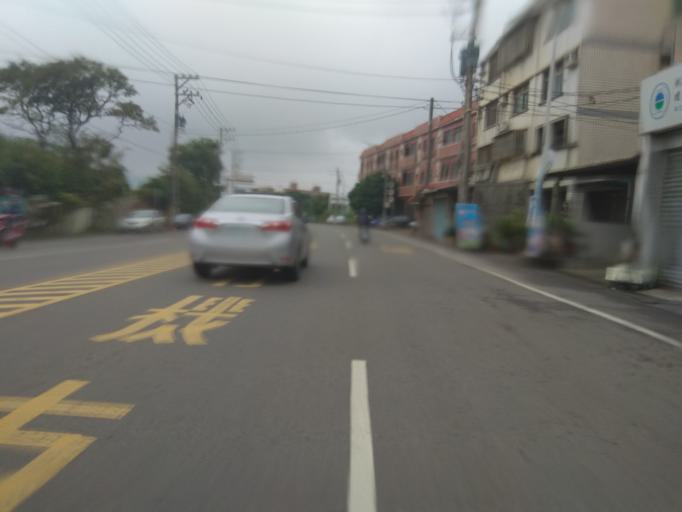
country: TW
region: Taiwan
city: Taoyuan City
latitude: 25.0307
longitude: 121.1042
